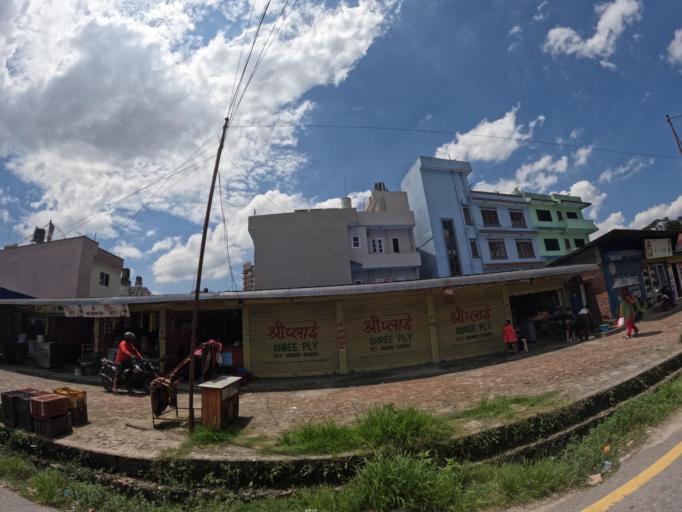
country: NP
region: Central Region
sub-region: Bagmati Zone
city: Kathmandu
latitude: 27.7557
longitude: 85.3278
